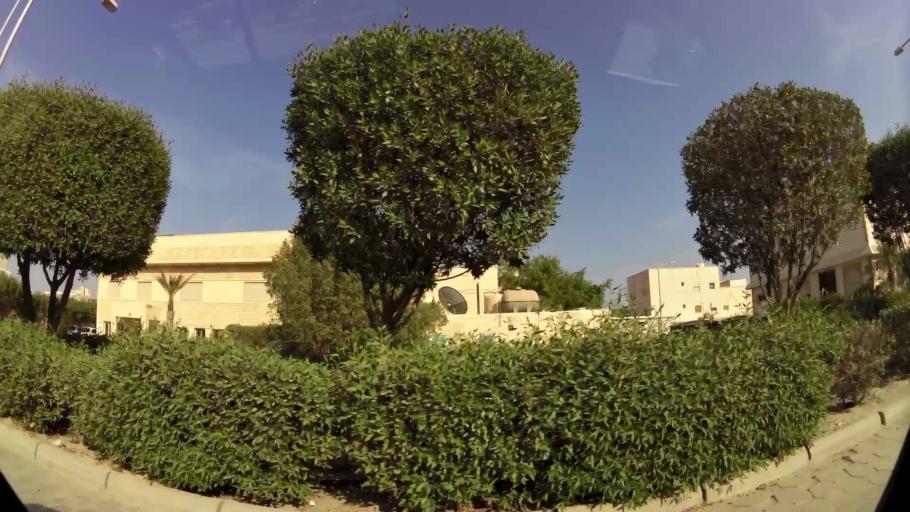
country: KW
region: Al Ahmadi
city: Ar Riqqah
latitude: 29.1521
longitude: 48.1049
